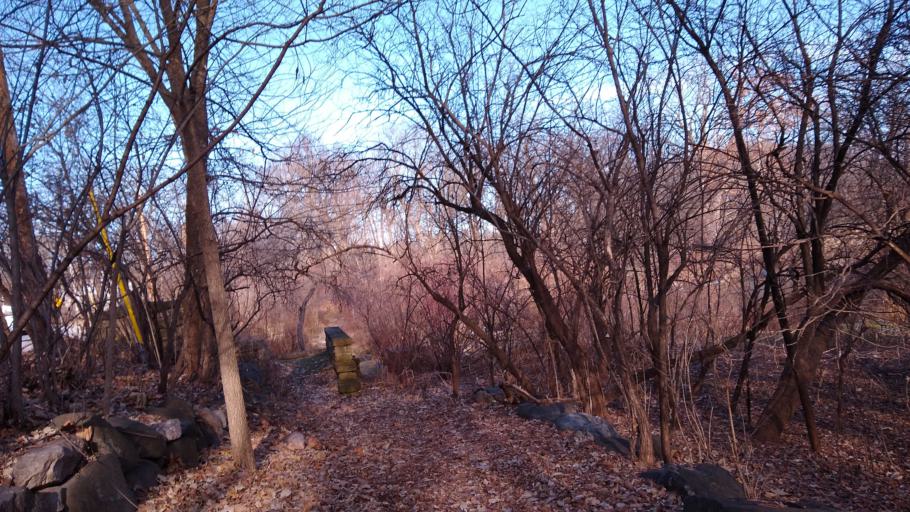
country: US
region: Wisconsin
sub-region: Dane County
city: Shorewood Hills
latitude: 43.0498
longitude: -89.4370
